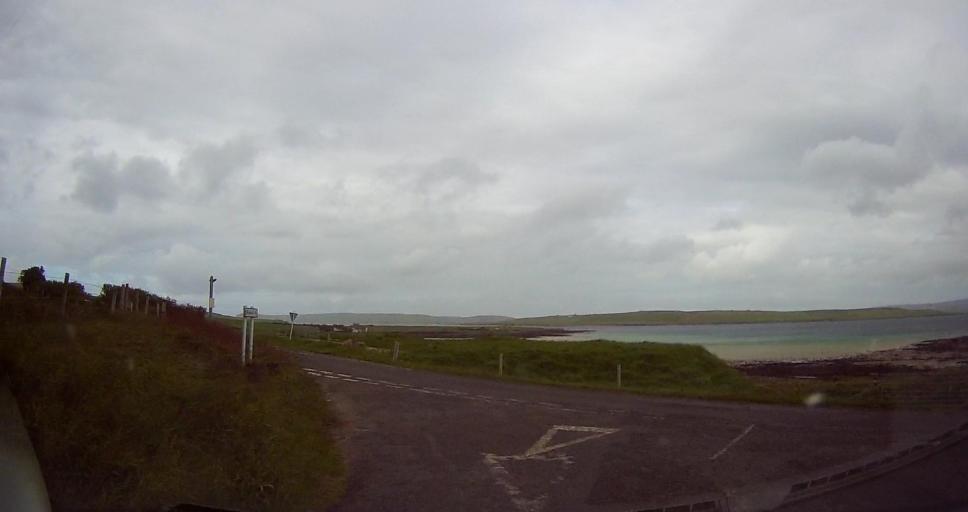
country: GB
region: Scotland
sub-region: Orkney Islands
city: Stromness
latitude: 58.9057
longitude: -3.3163
